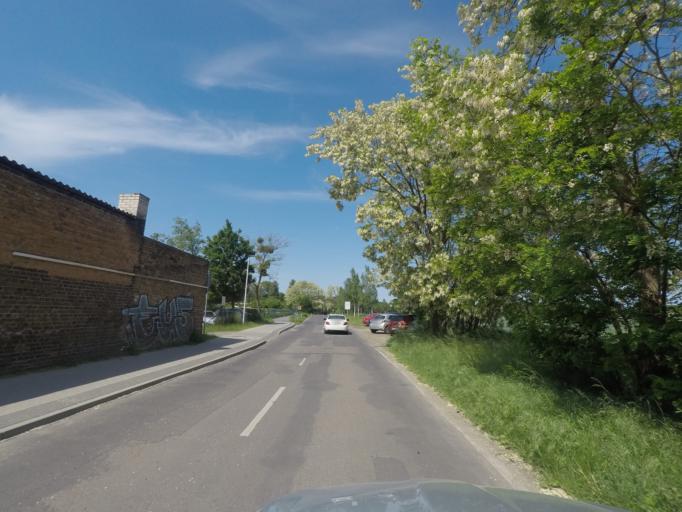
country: DE
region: Brandenburg
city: Melchow
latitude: 52.8501
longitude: 13.7269
